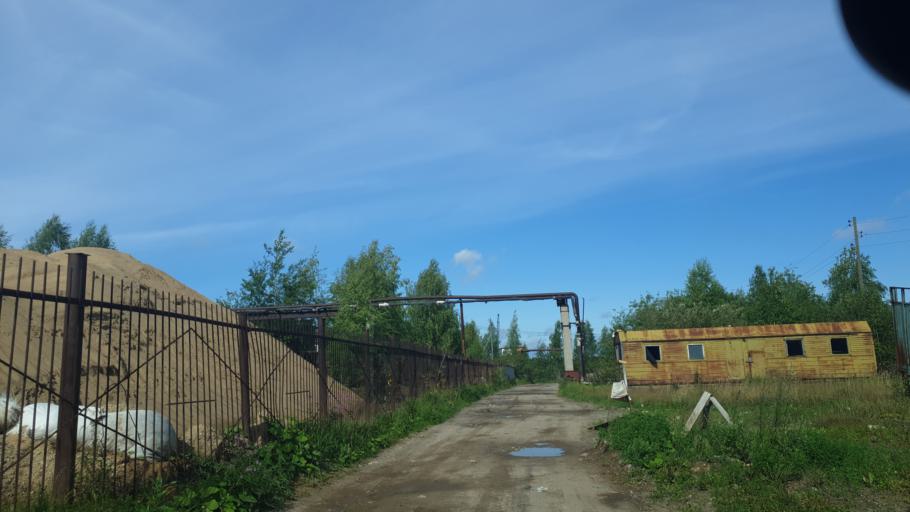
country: RU
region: Komi Republic
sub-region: Syktyvdinskiy Rayon
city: Syktyvkar
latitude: 61.7237
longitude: 50.7529
